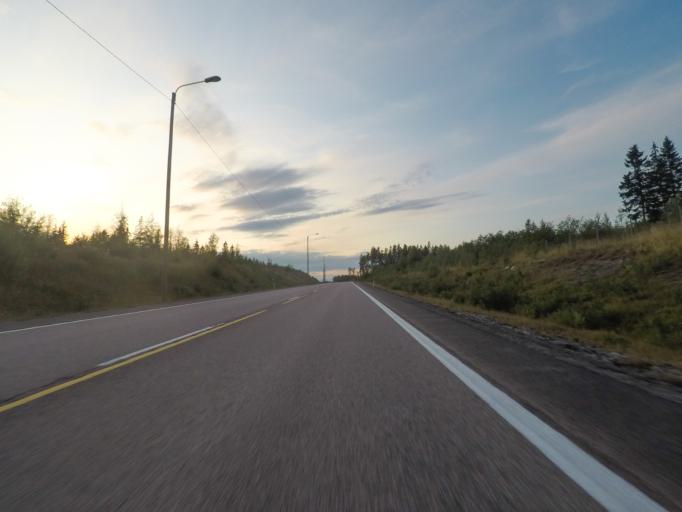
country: FI
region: Central Finland
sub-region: Jyvaeskylae
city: Toivakka
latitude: 62.1071
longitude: 25.9782
